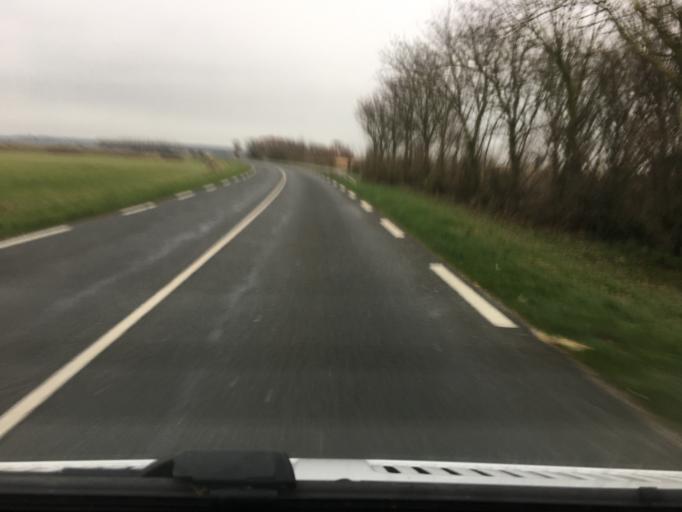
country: FR
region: Picardie
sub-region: Departement de la Somme
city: Pende
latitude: 50.1906
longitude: 1.5635
